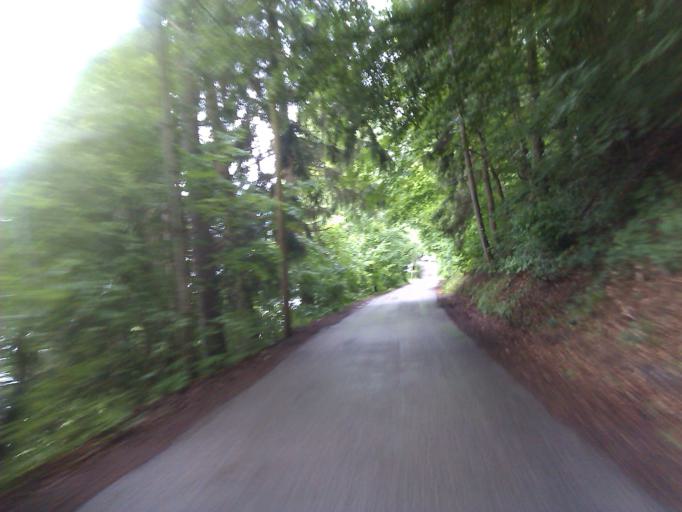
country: DE
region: Bavaria
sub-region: Swabia
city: Schwangau
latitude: 47.6103
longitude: 10.7197
